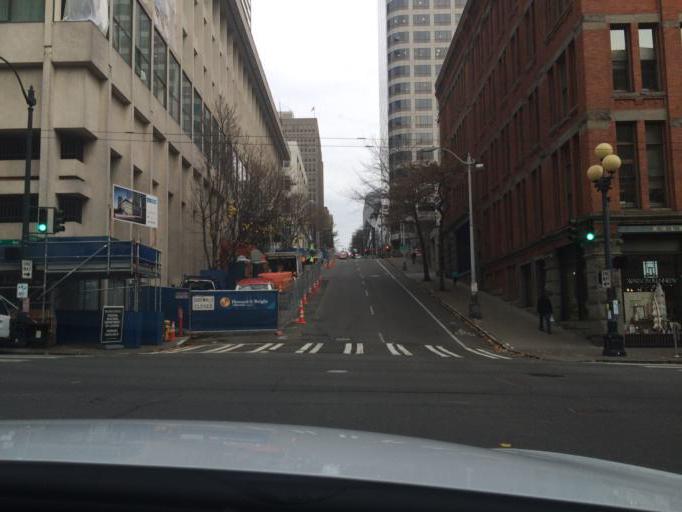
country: US
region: Washington
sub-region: King County
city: Seattle
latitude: 47.6054
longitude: -122.3371
